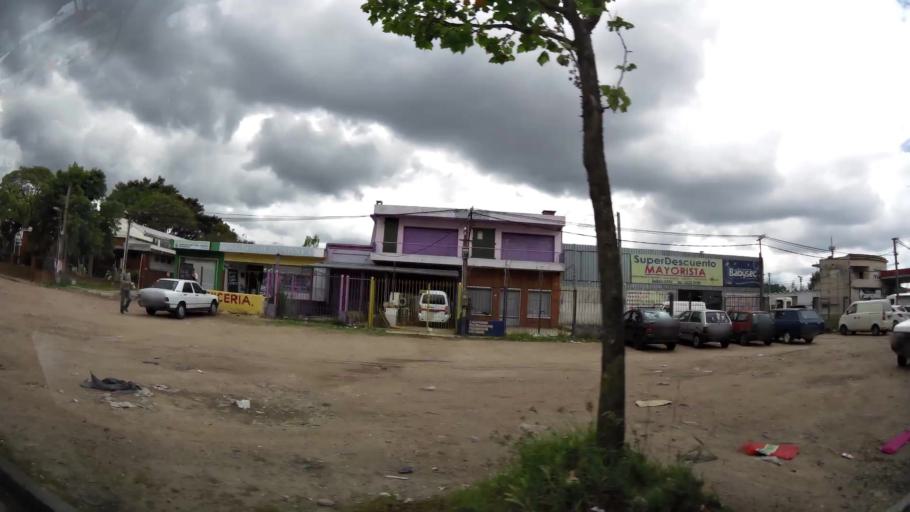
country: UY
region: Canelones
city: Toledo
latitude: -34.8238
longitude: -56.1405
